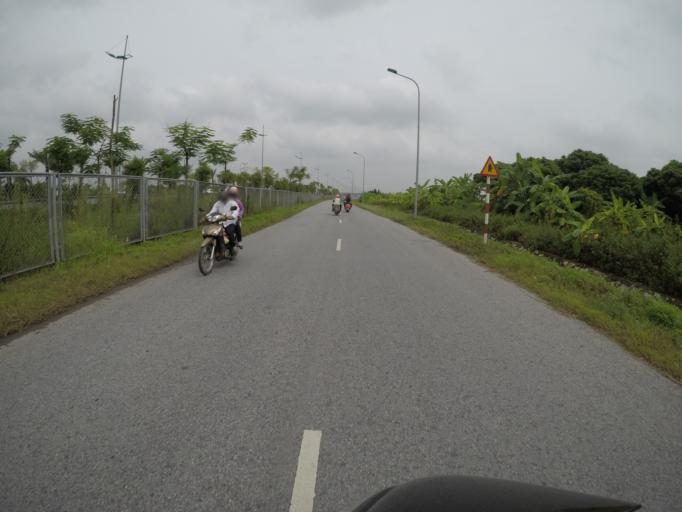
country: VN
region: Ha Noi
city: Dong Anh
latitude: 21.1592
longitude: 105.8198
